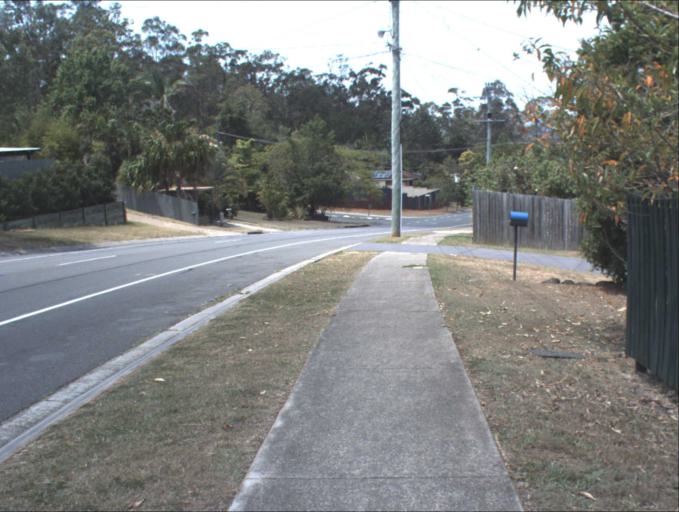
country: AU
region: Queensland
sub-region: Logan
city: Slacks Creek
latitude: -27.6628
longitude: 153.1922
